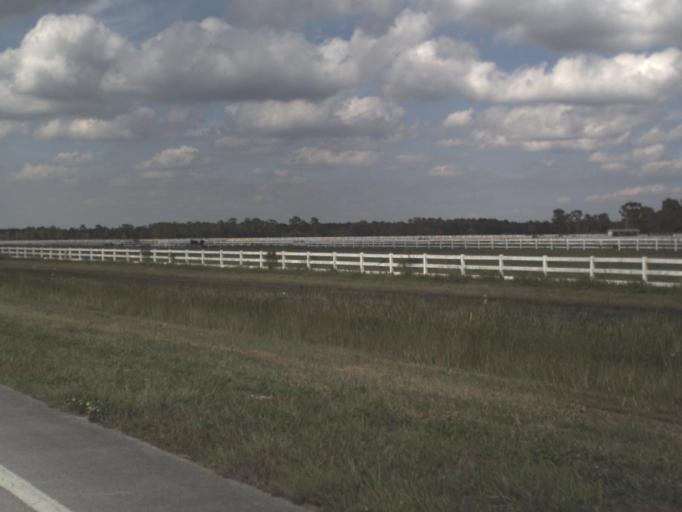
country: US
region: Florida
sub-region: Indian River County
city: Fellsmere
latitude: 27.5965
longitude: -80.8456
